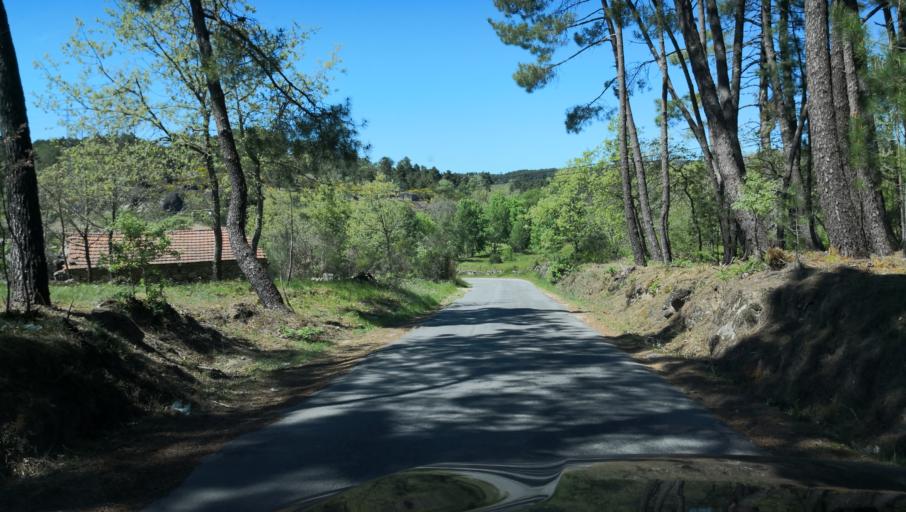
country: PT
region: Vila Real
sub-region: Vila Real
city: Vila Real
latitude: 41.2929
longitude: -7.6651
